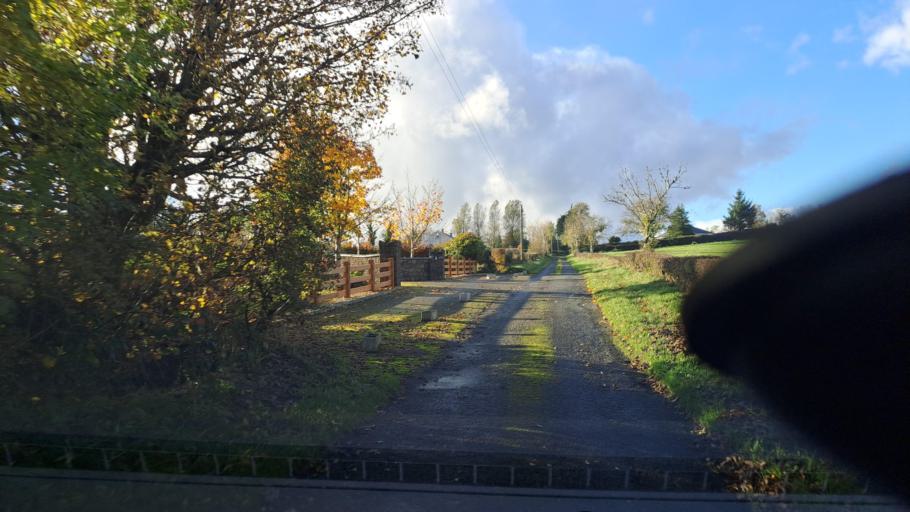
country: IE
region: Ulster
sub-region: An Cabhan
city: Bailieborough
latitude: 53.9333
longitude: -6.9444
